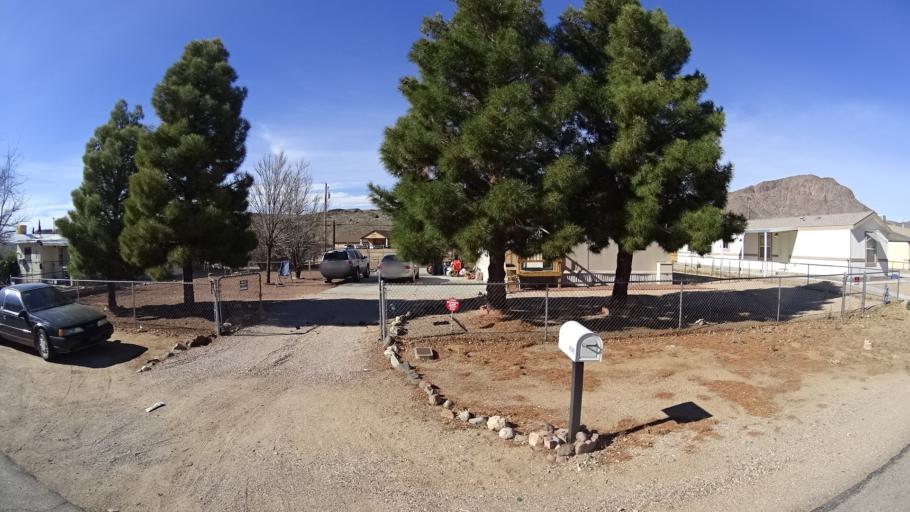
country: US
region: Arizona
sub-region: Mohave County
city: New Kingman-Butler
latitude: 35.2614
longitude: -114.0380
